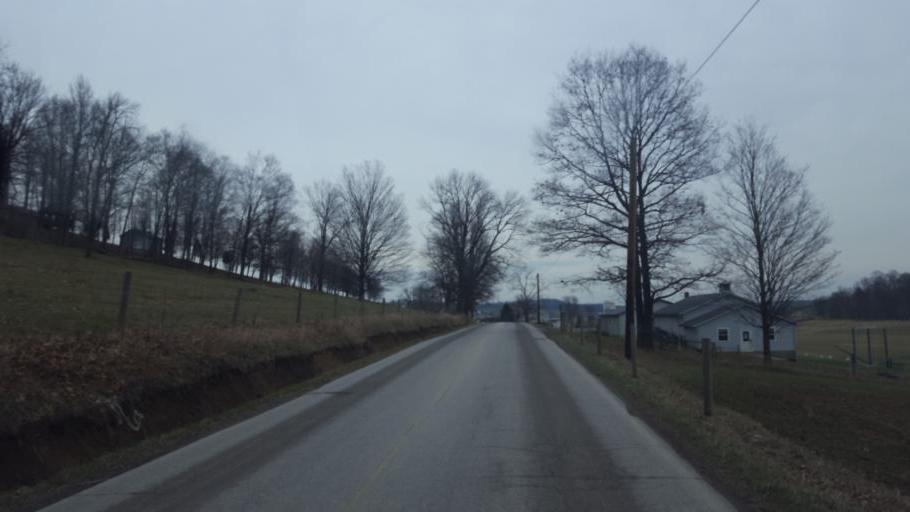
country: US
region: Ohio
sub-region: Tuscarawas County
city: Sugarcreek
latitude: 40.5250
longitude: -81.7298
